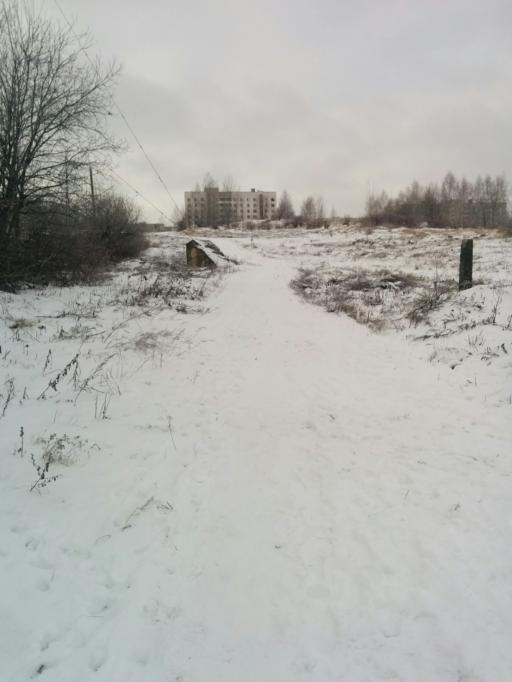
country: BY
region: Minsk
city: Novoye Medvezhino
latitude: 53.8951
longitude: 27.4593
